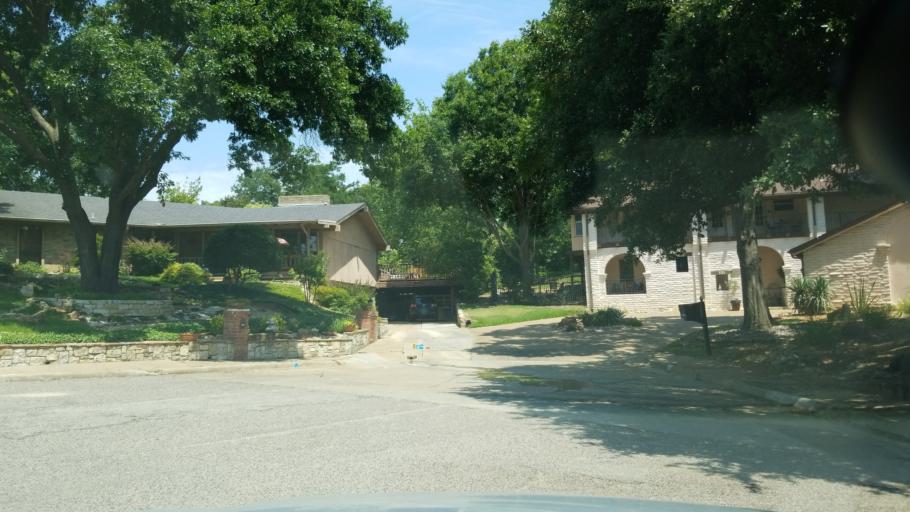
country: US
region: Texas
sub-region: Dallas County
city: Irving
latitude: 32.8504
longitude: -96.9412
